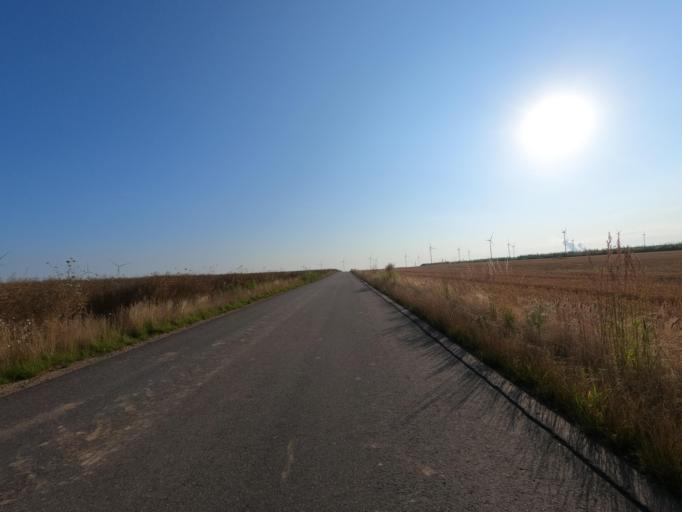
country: DE
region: North Rhine-Westphalia
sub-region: Regierungsbezirk Dusseldorf
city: Juchen
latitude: 51.0310
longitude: 6.4956
